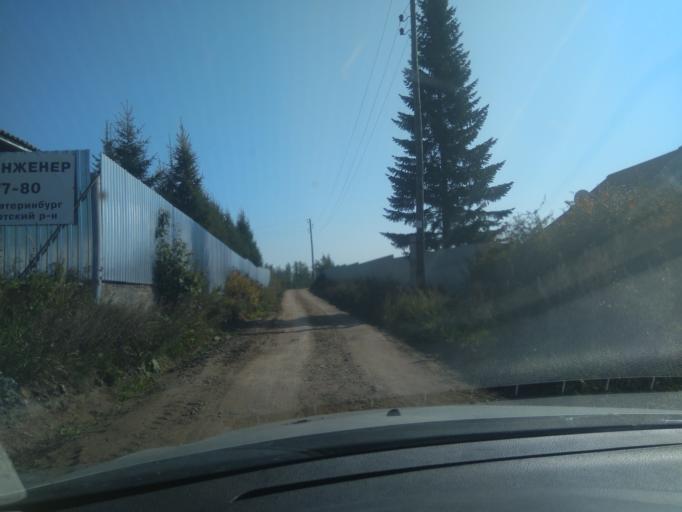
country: RU
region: Sverdlovsk
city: Pokrovskoye
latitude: 56.4365
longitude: 61.6006
